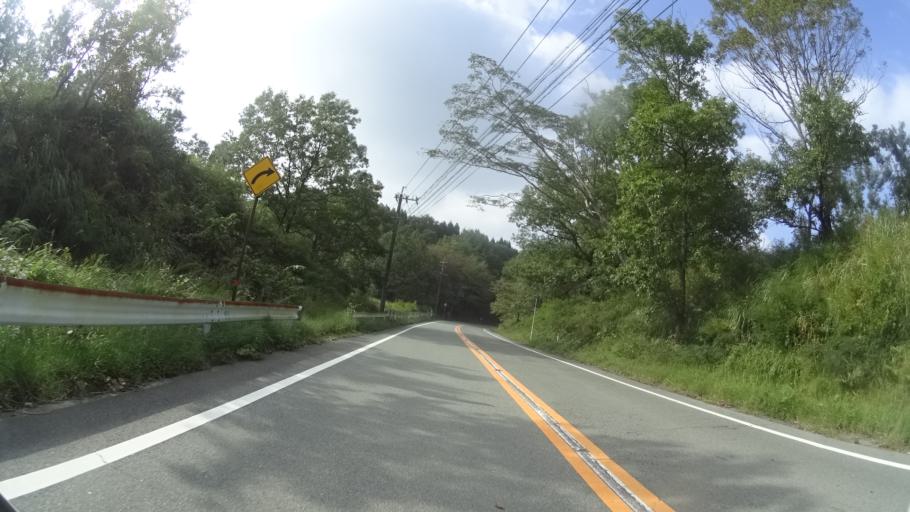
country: JP
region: Kumamoto
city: Aso
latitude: 33.0588
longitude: 131.0669
